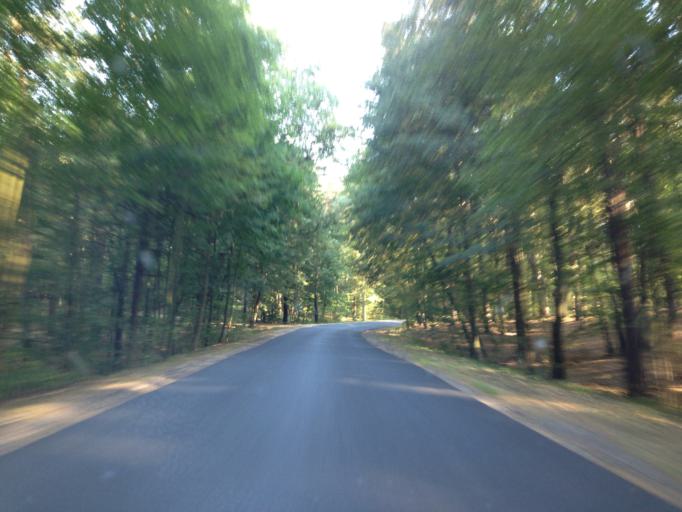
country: PL
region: Kujawsko-Pomorskie
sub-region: Powiat brodnicki
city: Brodnica
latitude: 53.3573
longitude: 19.3866
